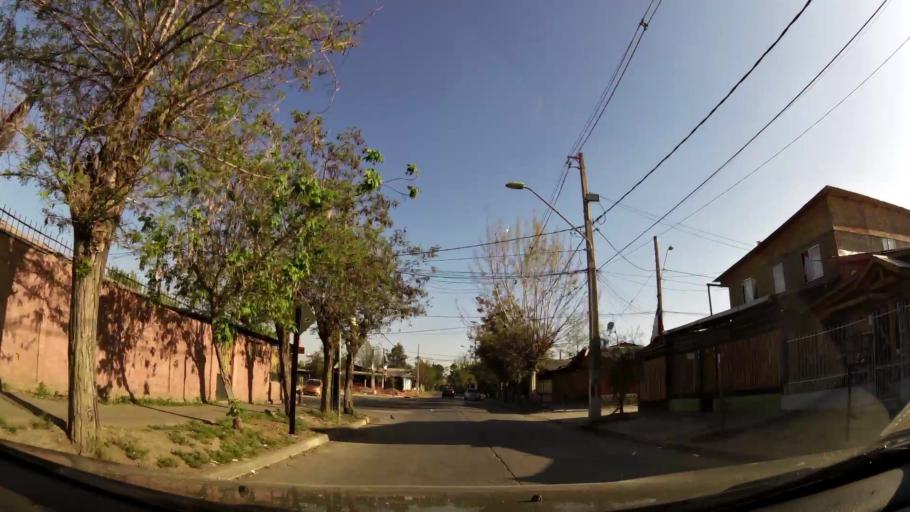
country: CL
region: Santiago Metropolitan
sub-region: Provincia de Santiago
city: La Pintana
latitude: -33.5836
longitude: -70.6605
